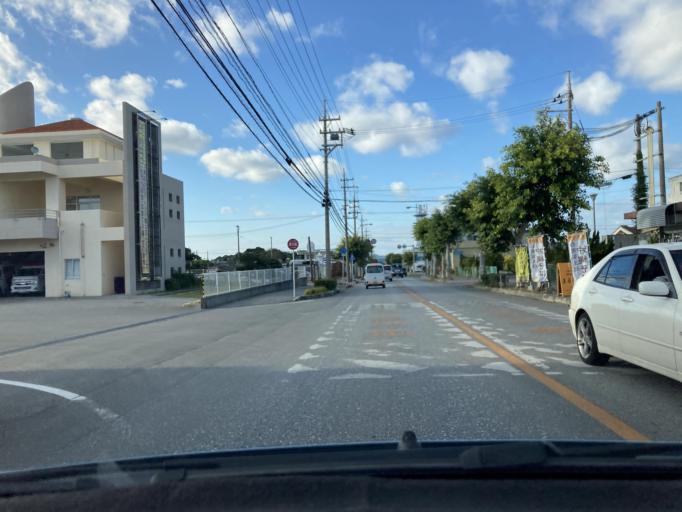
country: JP
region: Okinawa
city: Gushikawa
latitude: 26.3603
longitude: 127.8616
